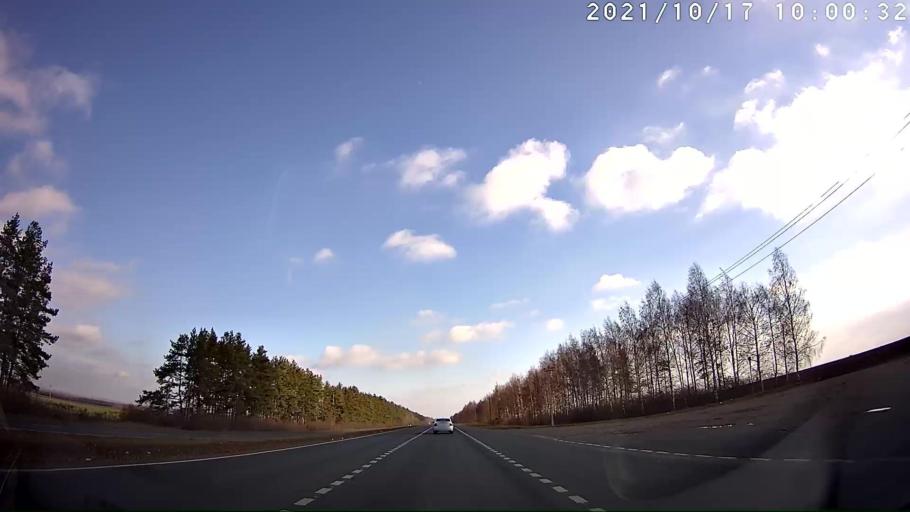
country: RU
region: Mariy-El
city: Yoshkar-Ola
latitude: 56.7243
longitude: 48.1216
